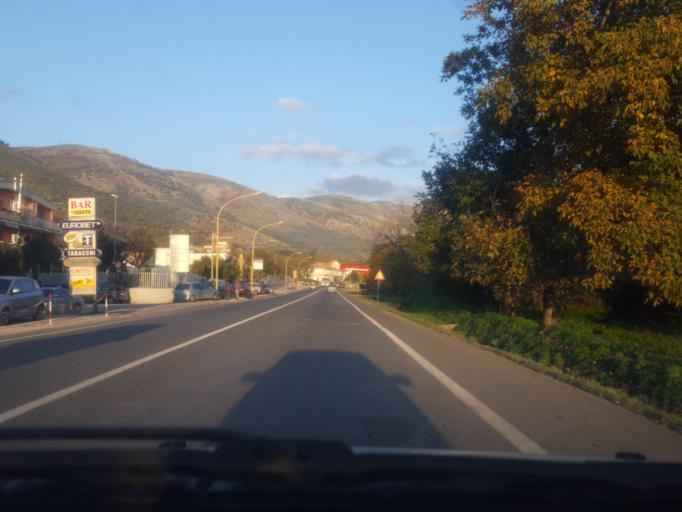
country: IT
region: Campania
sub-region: Provincia di Caserta
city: Arienzo
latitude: 41.0321
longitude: 14.4963
